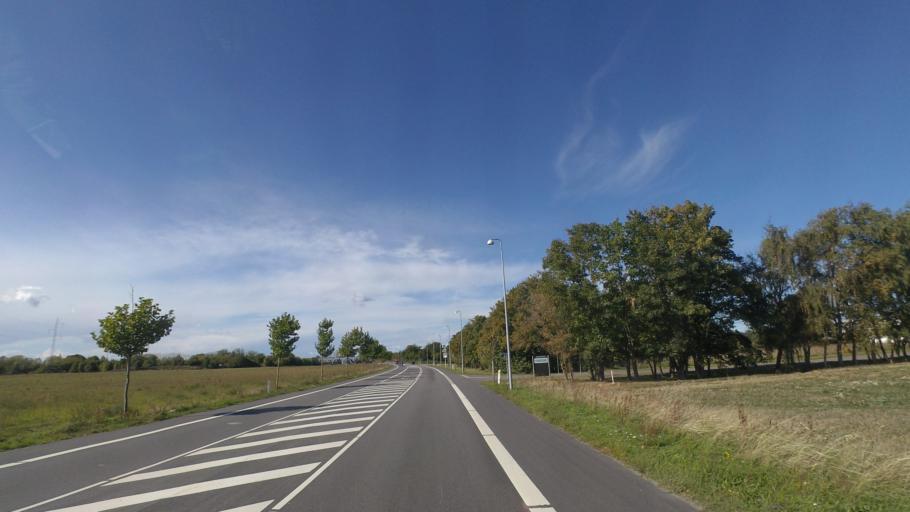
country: DK
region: Capital Region
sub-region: Bornholm Kommune
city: Ronne
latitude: 55.0901
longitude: 14.7375
